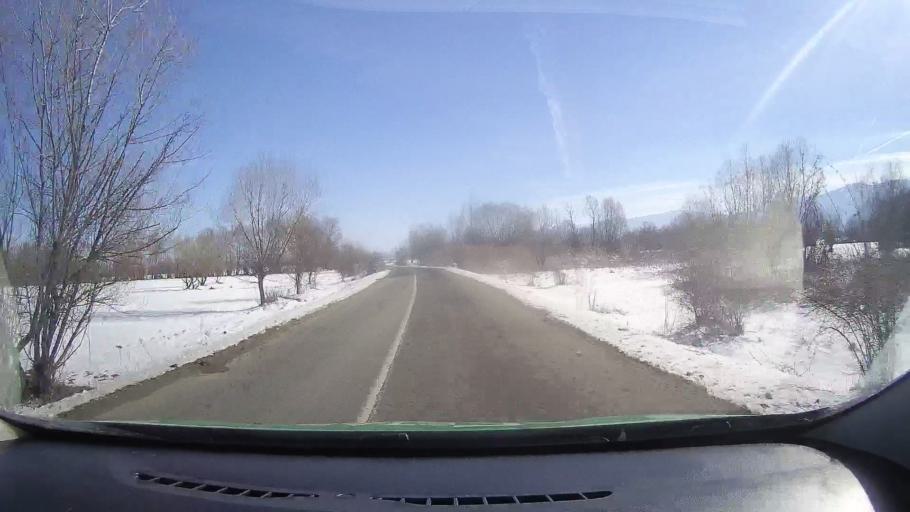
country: RO
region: Brasov
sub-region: Comuna Harseni
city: Harseni
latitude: 45.7292
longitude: 24.9767
